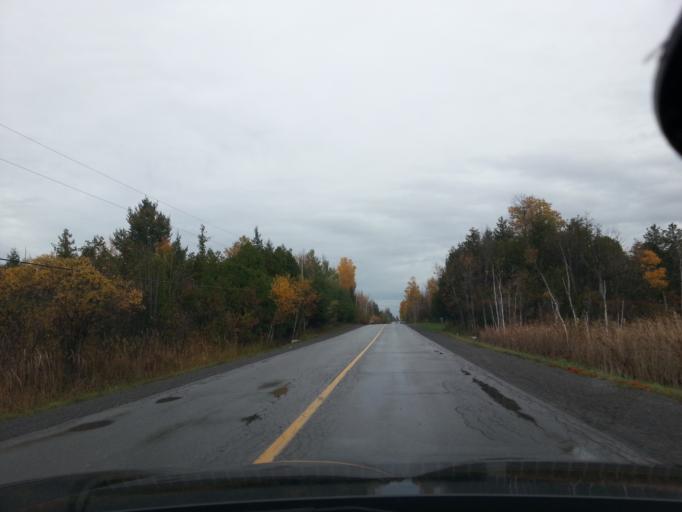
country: CA
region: Ontario
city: Bells Corners
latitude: 45.2337
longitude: -75.9349
